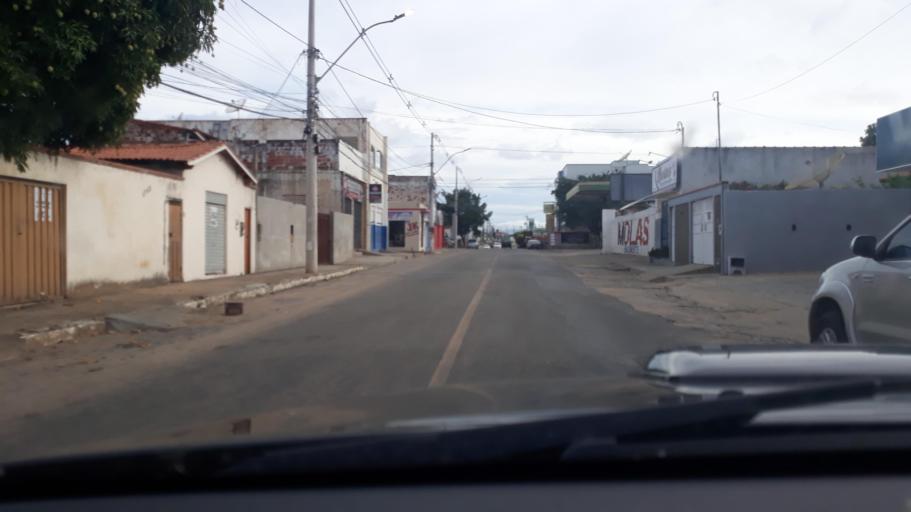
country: BR
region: Bahia
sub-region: Guanambi
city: Guanambi
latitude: -14.2119
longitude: -42.7712
